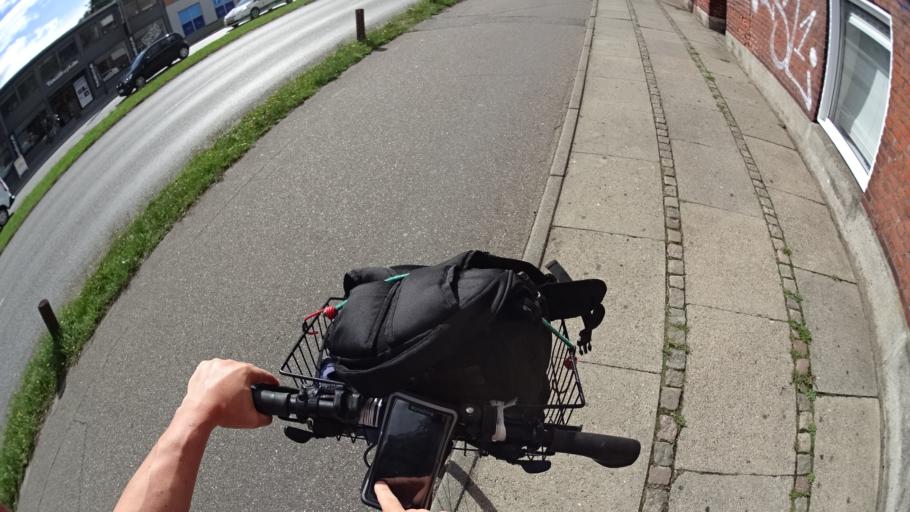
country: DK
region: Central Jutland
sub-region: Arhus Kommune
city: Arhus
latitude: 56.1563
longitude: 10.1809
